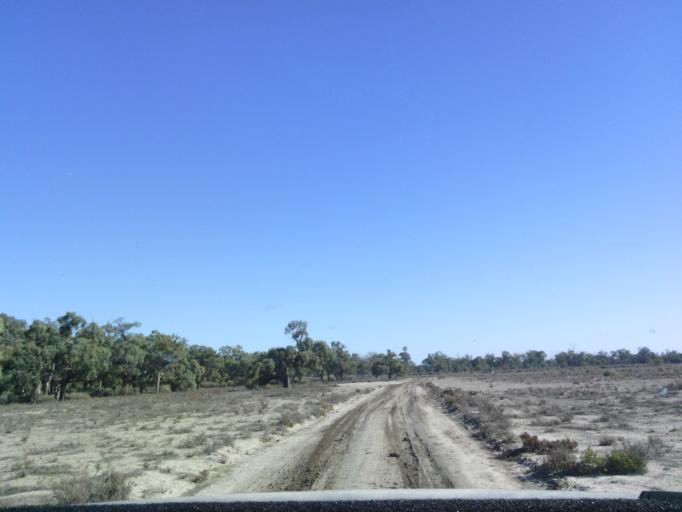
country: AU
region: South Australia
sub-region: Renmark Paringa
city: Renmark West
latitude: -34.2601
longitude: 140.6947
